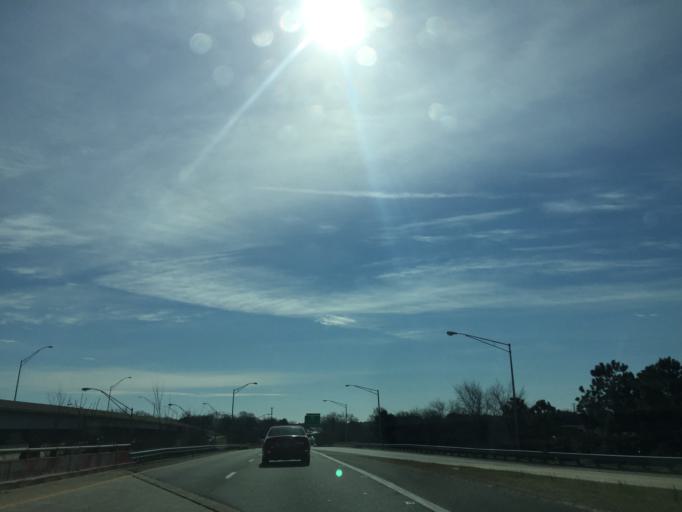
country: US
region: Virginia
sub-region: City of Norfolk
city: Norfolk
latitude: 36.9177
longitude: -76.2686
